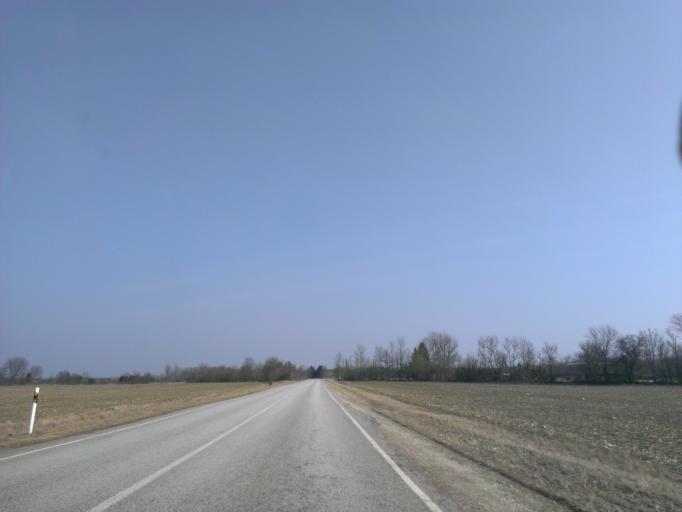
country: EE
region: Saare
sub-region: Kuressaare linn
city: Kuressaare
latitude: 58.2863
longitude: 22.6552
